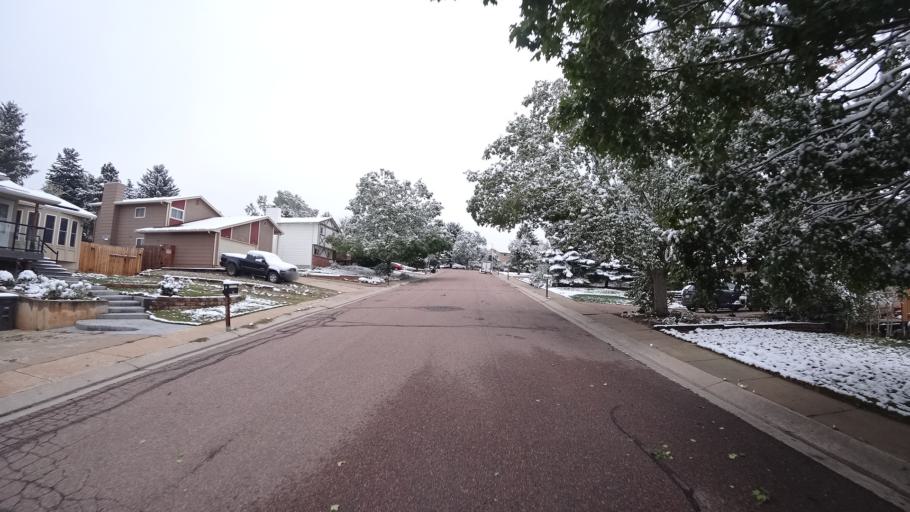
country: US
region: Colorado
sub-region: El Paso County
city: Colorado Springs
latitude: 38.9178
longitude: -104.7773
